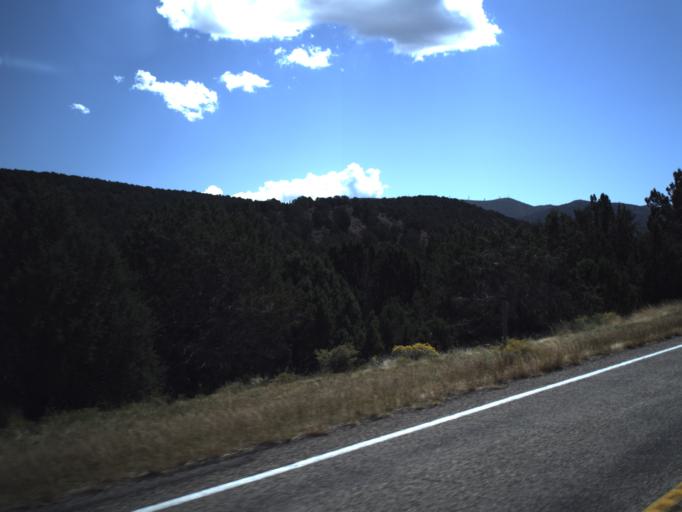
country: US
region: Utah
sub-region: Washington County
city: Enterprise
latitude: 37.5605
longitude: -113.6910
